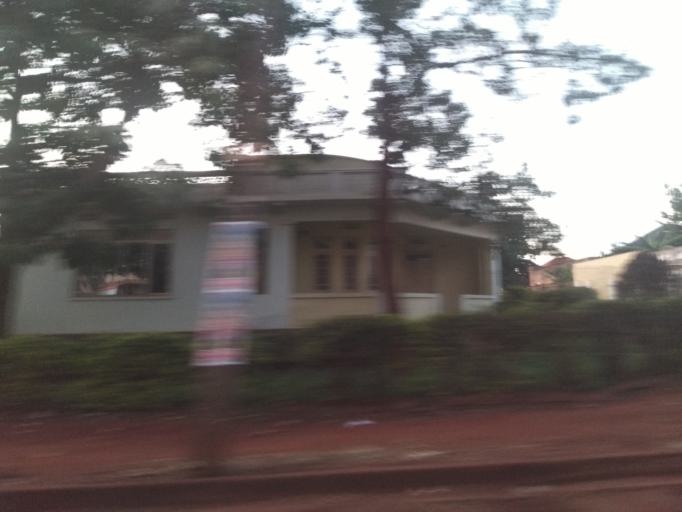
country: UG
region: Eastern Region
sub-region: Jinja District
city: Jinja
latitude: 0.4330
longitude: 33.2080
